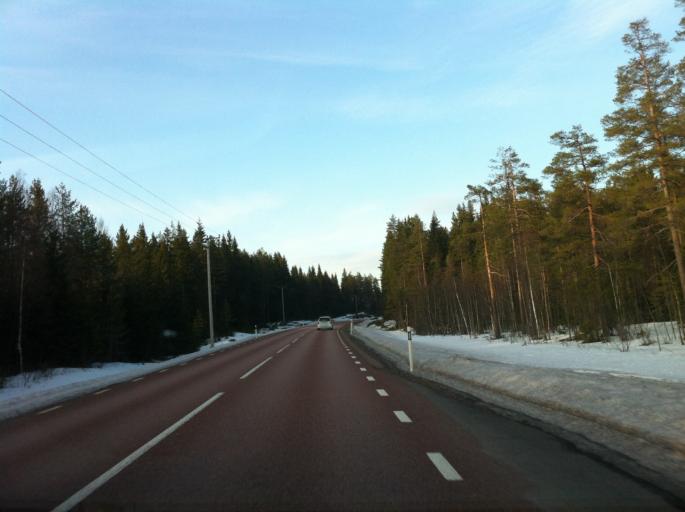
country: SE
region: Dalarna
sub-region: Vansbro Kommun
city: Vansbro
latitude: 60.2725
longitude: 14.1703
